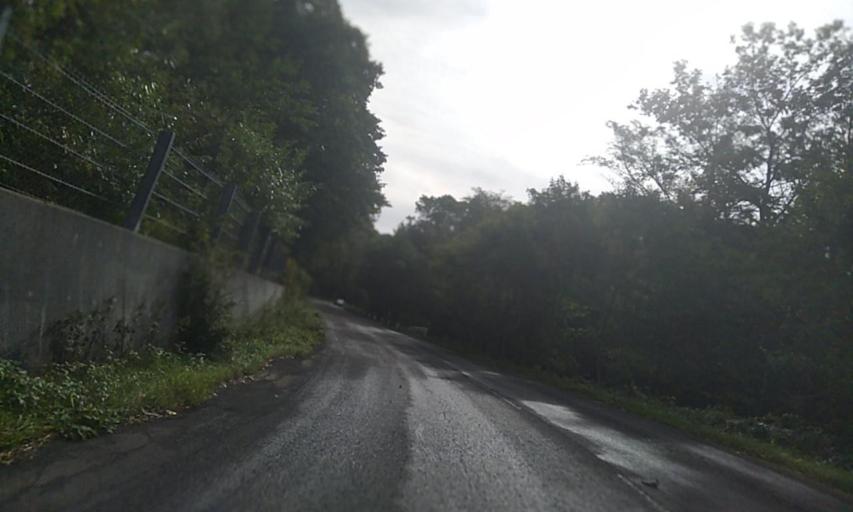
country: JP
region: Hokkaido
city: Abashiri
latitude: 43.6792
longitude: 144.5444
